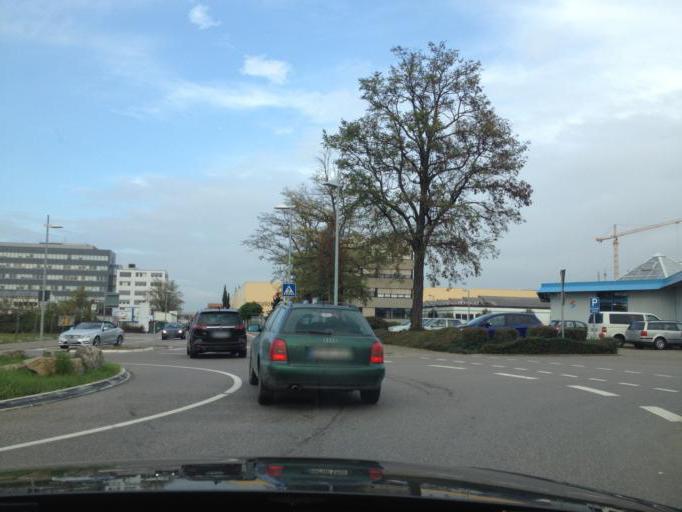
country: DE
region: Baden-Wuerttemberg
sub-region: Regierungsbezirk Stuttgart
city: Neckarsulm
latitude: 49.1742
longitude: 9.2214
